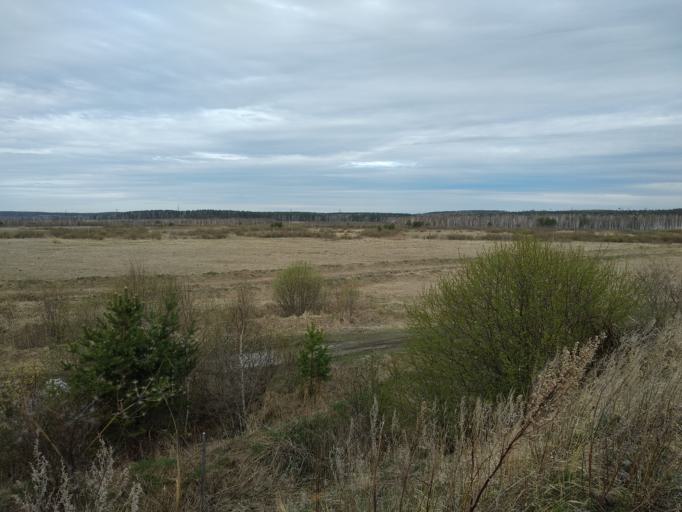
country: RU
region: Sverdlovsk
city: Beryozovsky
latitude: 56.9206
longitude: 60.7360
